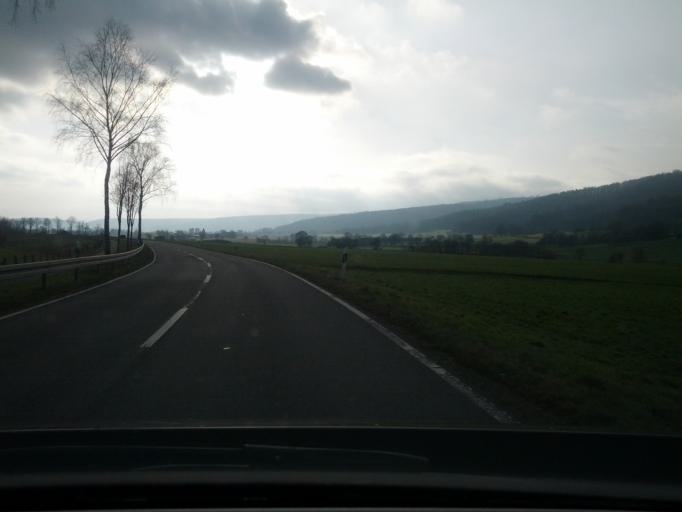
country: DE
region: Lower Saxony
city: Buhren
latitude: 51.5172
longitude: 9.5838
